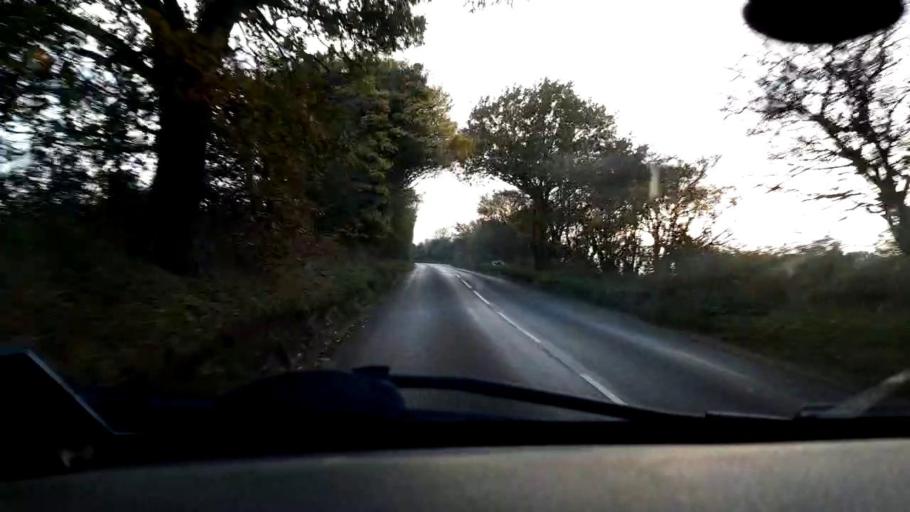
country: GB
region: England
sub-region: Norfolk
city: Mattishall
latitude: 52.7102
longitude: 1.1075
